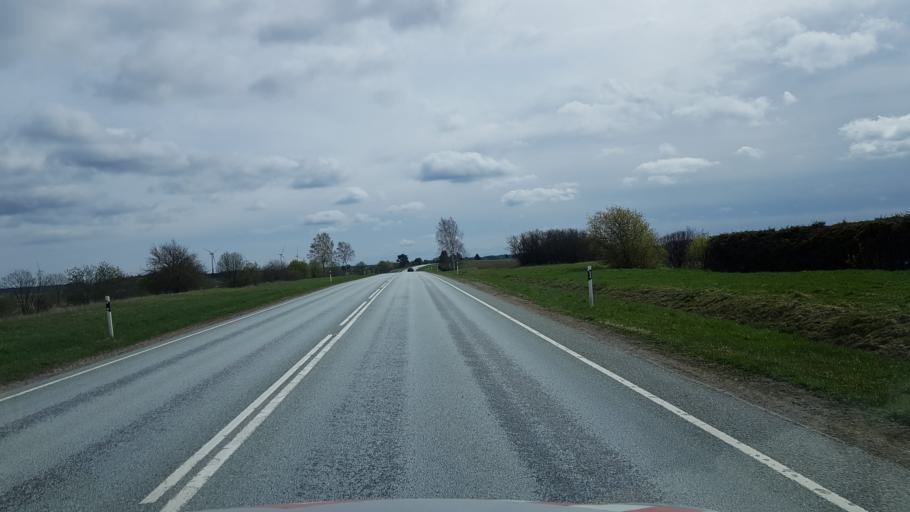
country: EE
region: Ida-Virumaa
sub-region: Aseri vald
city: Aseri
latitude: 59.4450
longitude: 26.7674
